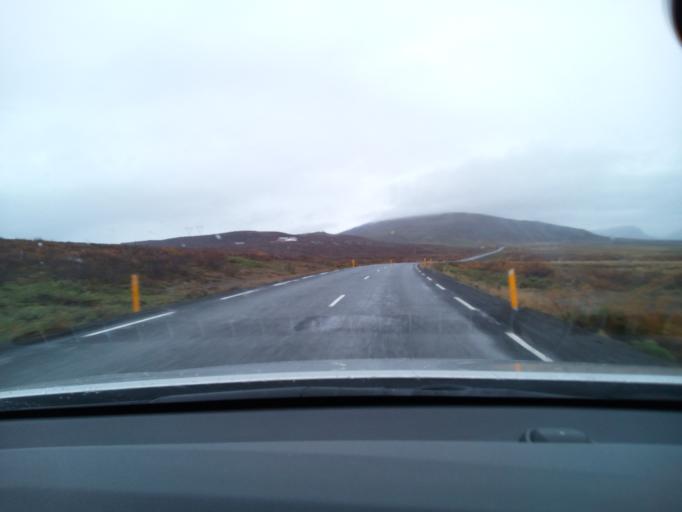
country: IS
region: Capital Region
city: Mosfellsbaer
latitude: 64.4096
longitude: -21.6491
